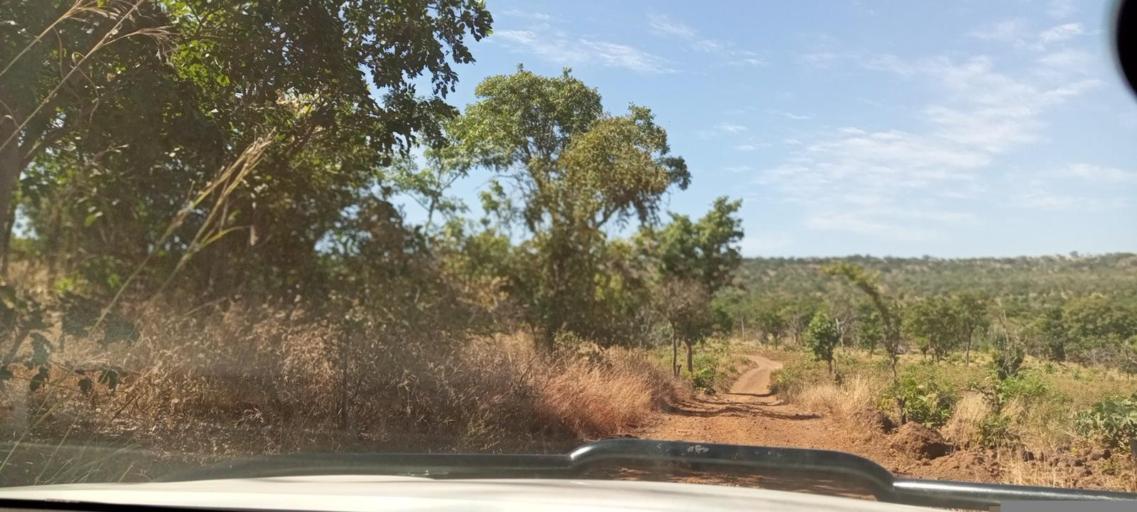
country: ML
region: Koulikoro
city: Kangaba
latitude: 12.3272
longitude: -8.6730
